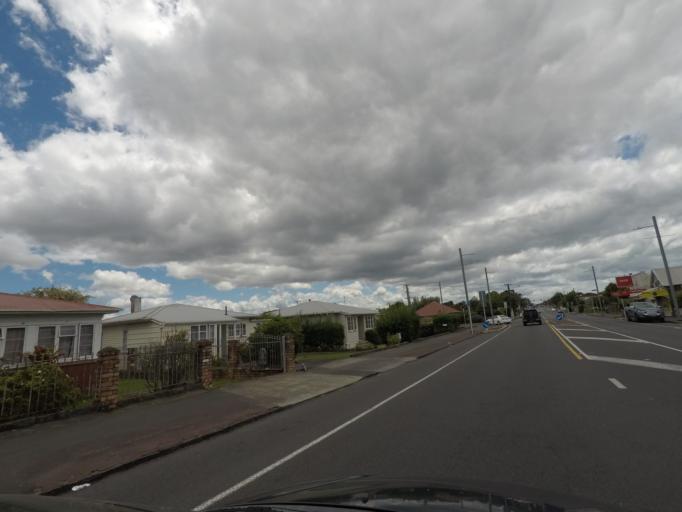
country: NZ
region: Auckland
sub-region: Auckland
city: Auckland
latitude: -36.8910
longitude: 174.7365
